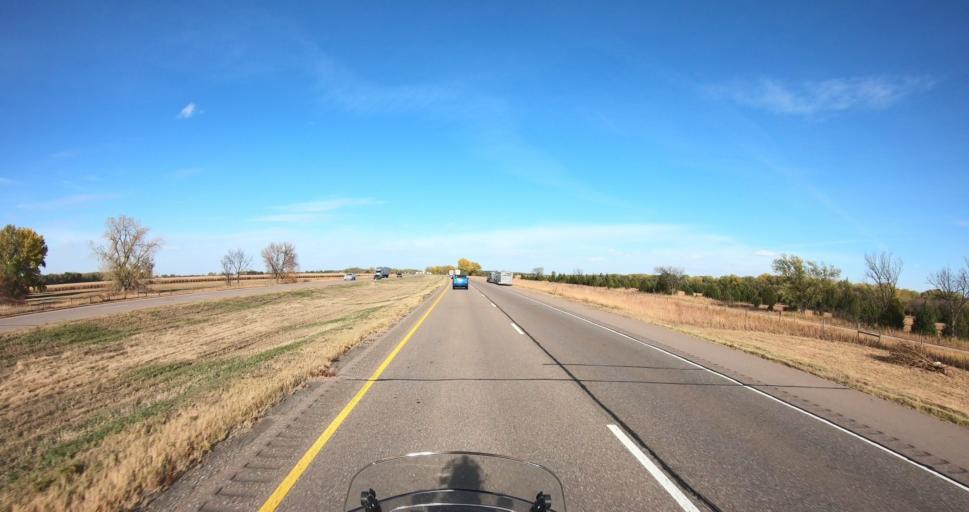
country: US
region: Nebraska
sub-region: Hall County
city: Wood River
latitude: 40.7438
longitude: -98.6288
